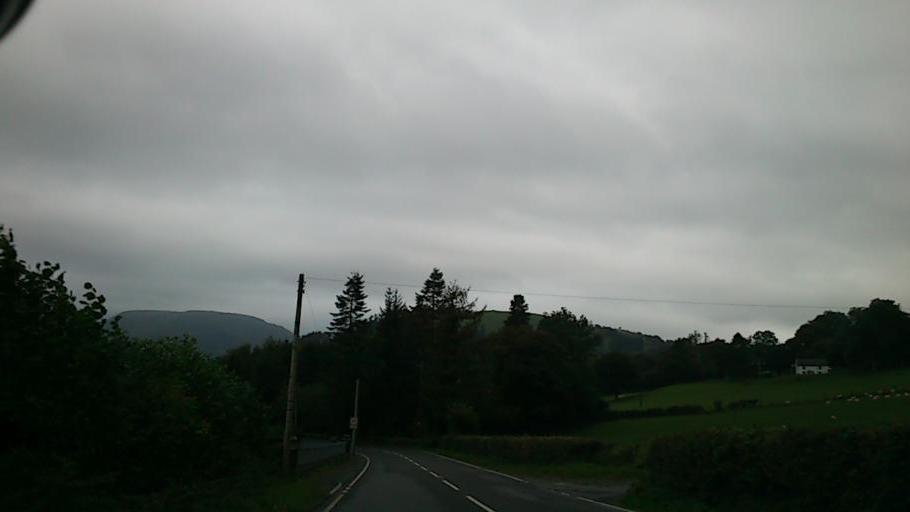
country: GB
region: Wales
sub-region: Gwynedd
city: Corris
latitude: 52.6943
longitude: -3.6836
